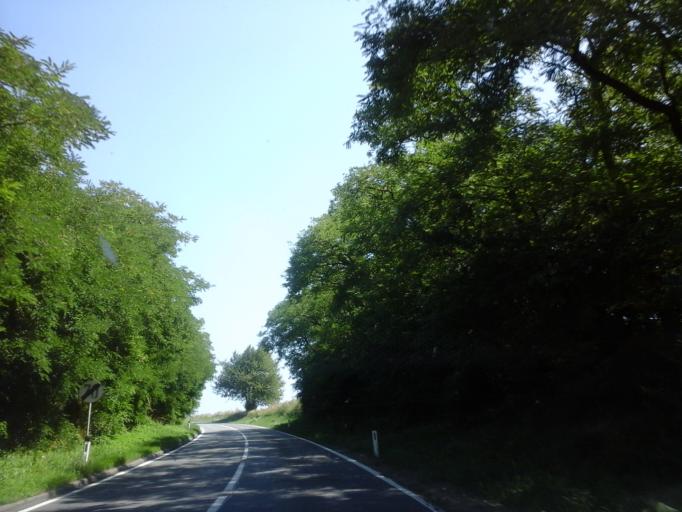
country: AT
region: Burgenland
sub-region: Politischer Bezirk Neusiedl am See
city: Edelstal
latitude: 48.0877
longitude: 16.9865
